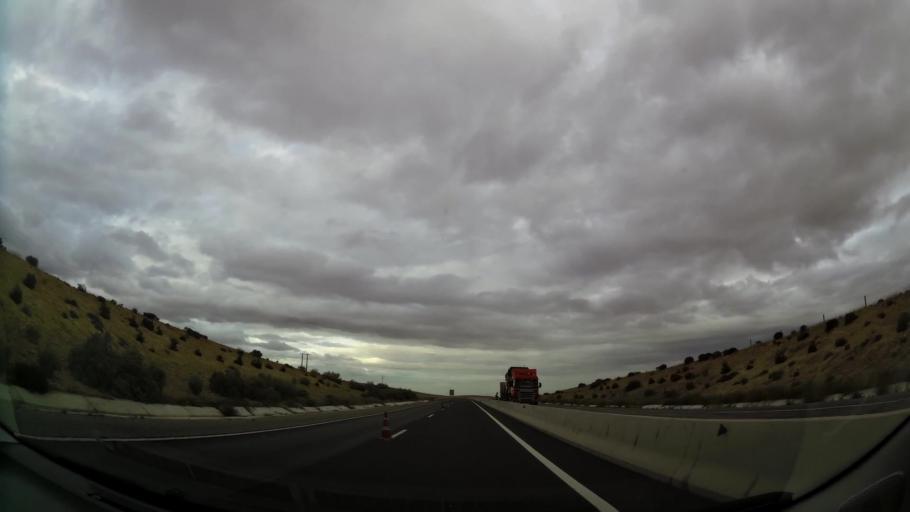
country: MA
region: Taza-Al Hoceima-Taounate
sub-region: Taza
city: Taza
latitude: 34.3077
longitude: -3.7038
